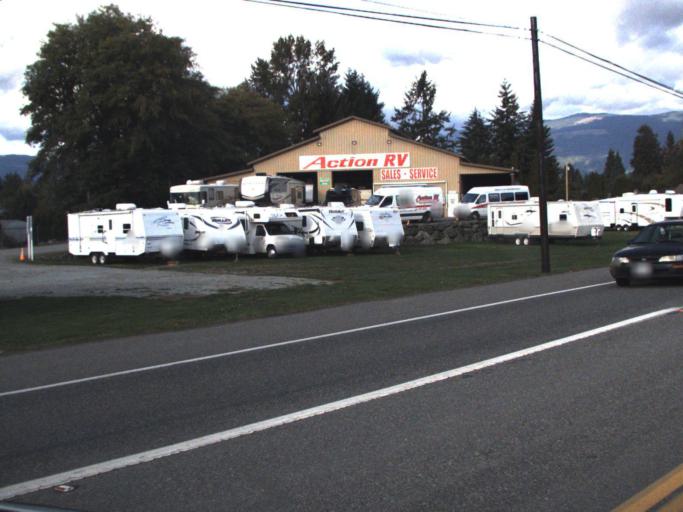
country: US
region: Washington
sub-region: Skagit County
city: Burlington
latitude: 48.4887
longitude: -122.2907
